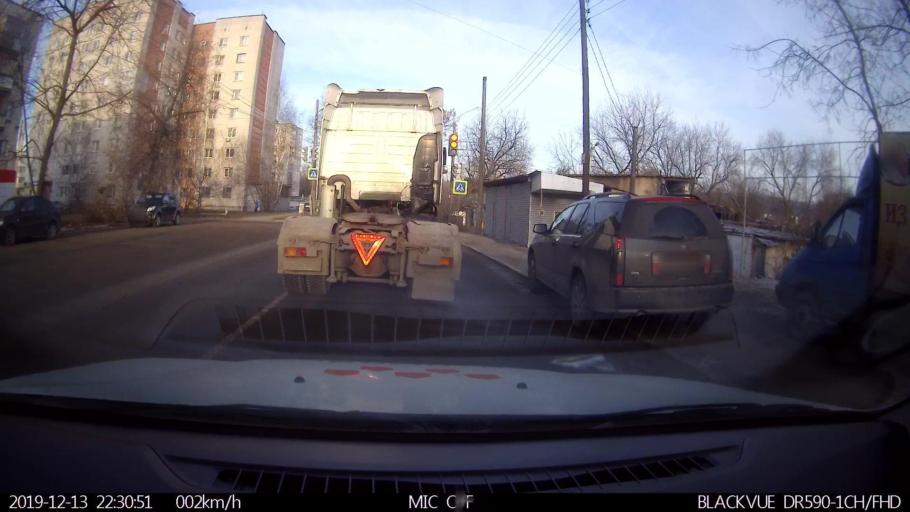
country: RU
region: Nizjnij Novgorod
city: Nizhniy Novgorod
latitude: 56.2797
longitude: 43.9522
